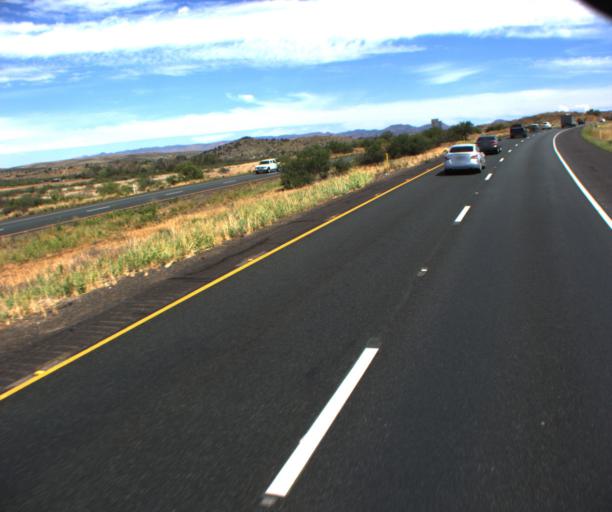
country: US
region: Arizona
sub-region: Yavapai County
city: Cordes Lakes
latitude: 34.4100
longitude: -112.0702
